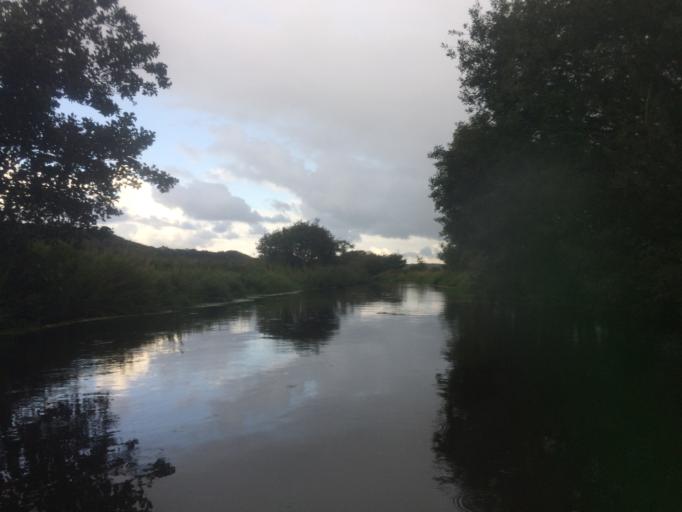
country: DK
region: South Denmark
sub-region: Vejle Kommune
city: Egtved
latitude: 55.6694
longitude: 9.3425
